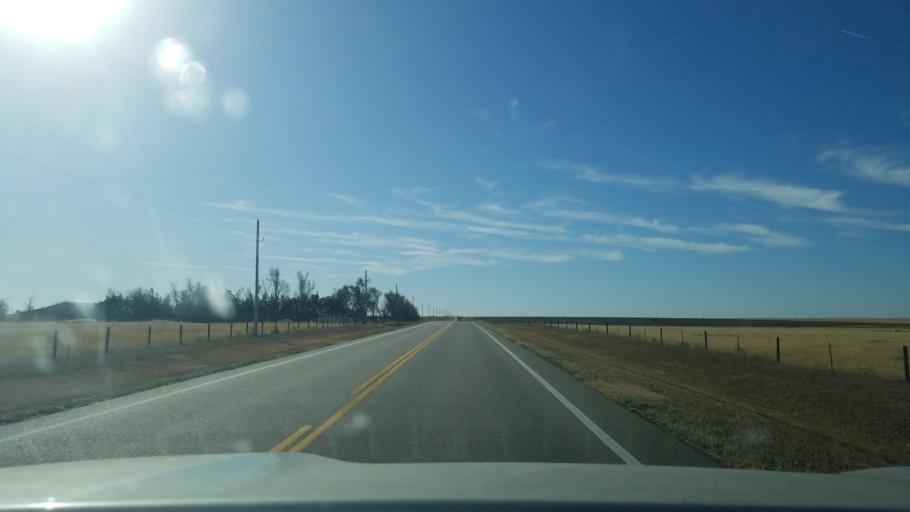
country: US
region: Kansas
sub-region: Ness County
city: Ness City
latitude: 38.4037
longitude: -99.8984
